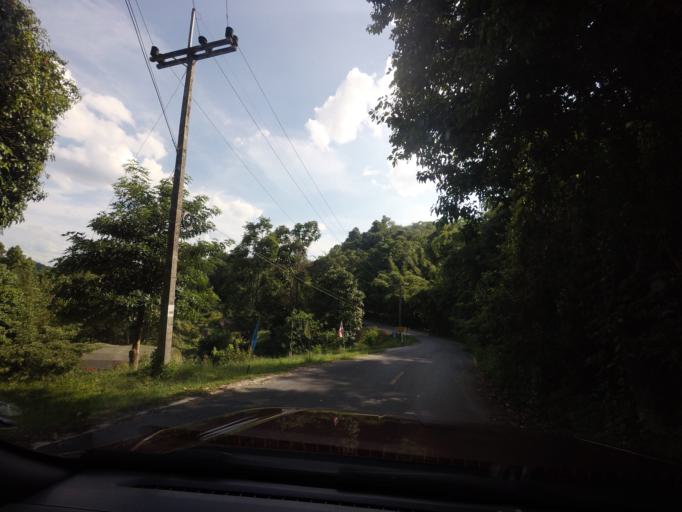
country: TH
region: Yala
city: Than To
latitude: 6.0669
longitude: 101.3663
